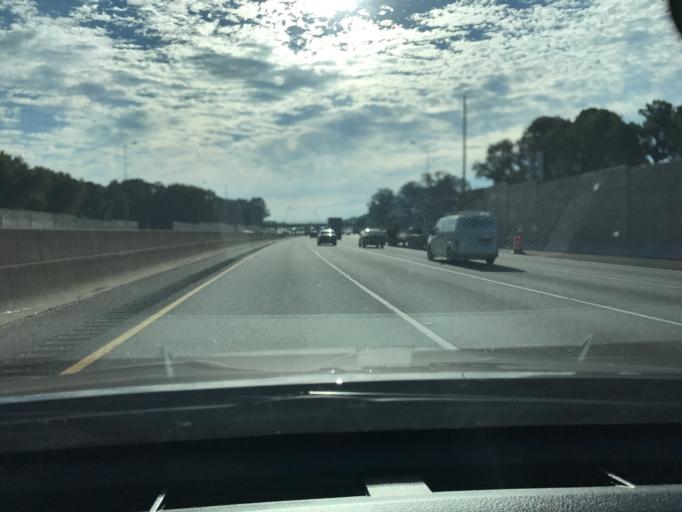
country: US
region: Georgia
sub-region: DeKalb County
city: Panthersville
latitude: 33.6989
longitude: -84.2761
